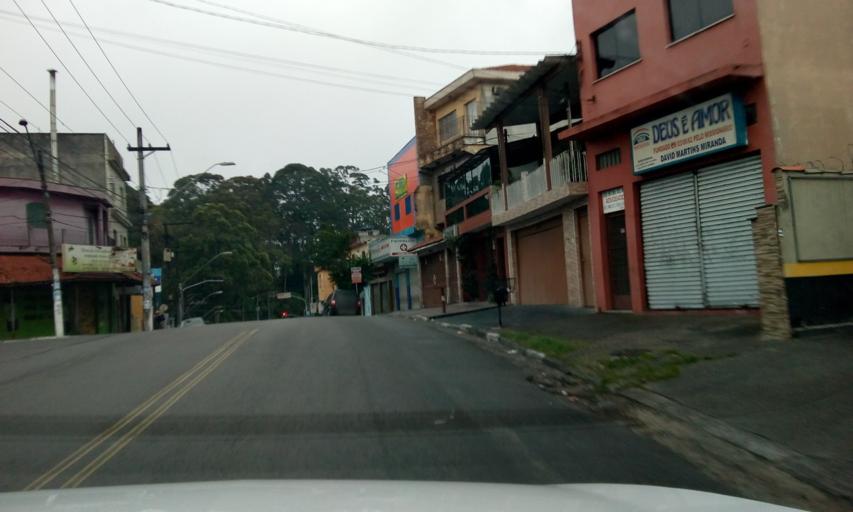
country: BR
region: Sao Paulo
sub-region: Diadema
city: Diadema
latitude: -23.6961
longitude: -46.6276
